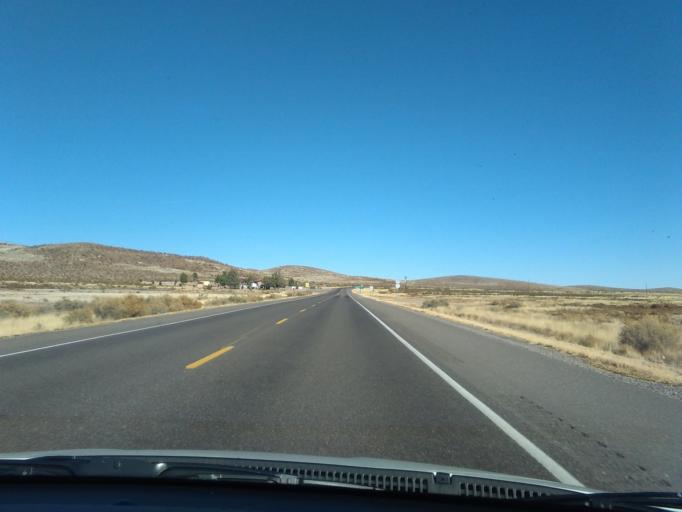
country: US
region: New Mexico
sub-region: Dona Ana County
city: Hatch
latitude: 32.5732
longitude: -107.4541
